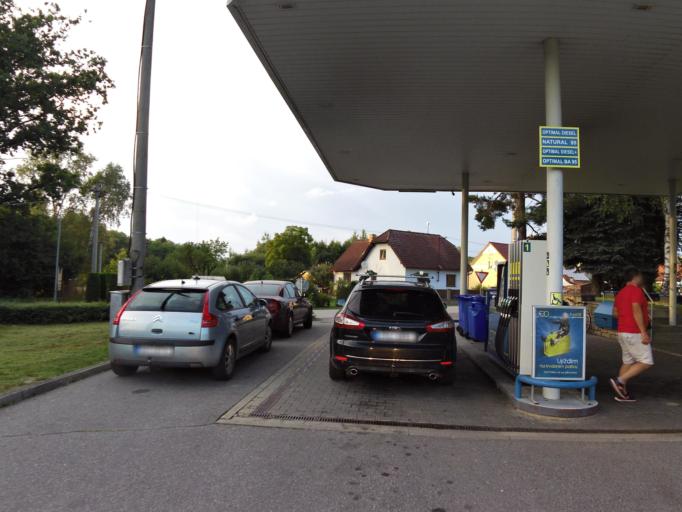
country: CZ
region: Jihocesky
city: Chlum u Trebone
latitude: 48.9501
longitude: 14.9213
